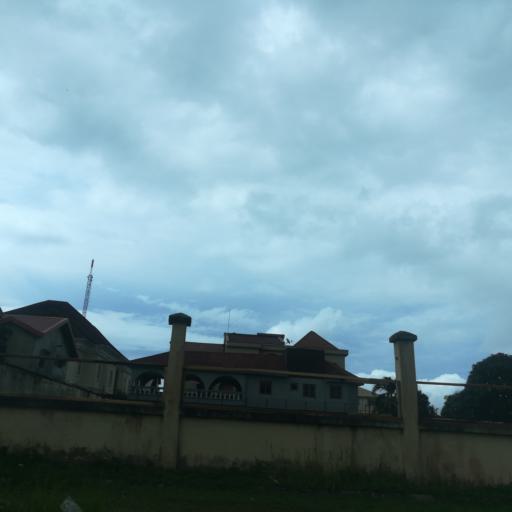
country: NG
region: Lagos
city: Ikoyi
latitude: 6.4406
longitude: 3.4619
